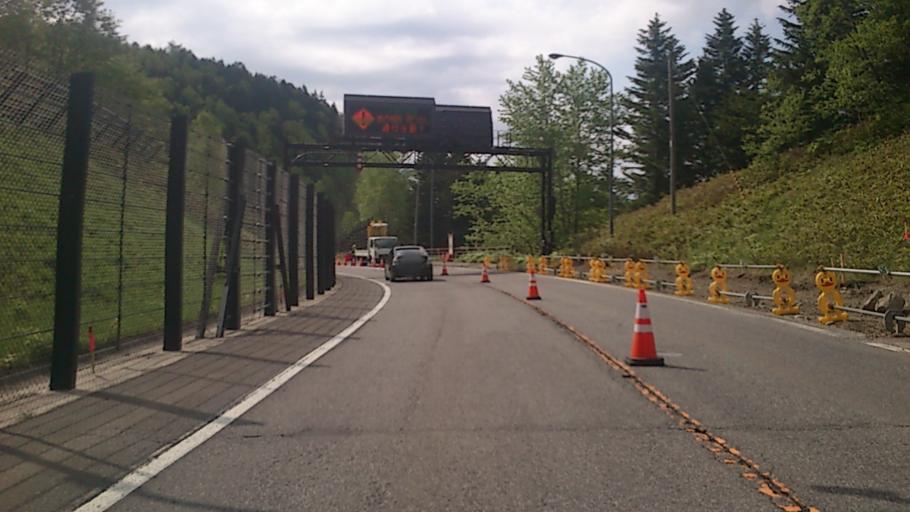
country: JP
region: Hokkaido
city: Kamikawa
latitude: 43.6821
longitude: 143.0355
